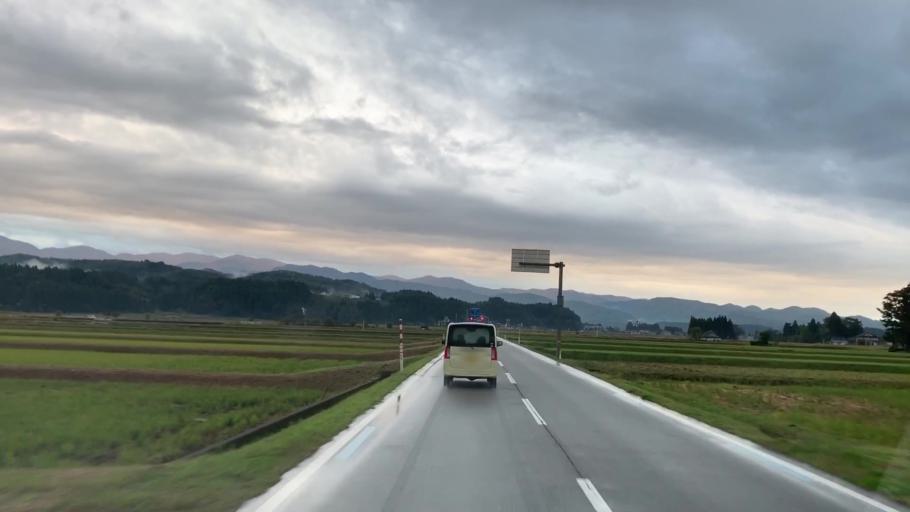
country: JP
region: Toyama
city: Kamiichi
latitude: 36.6289
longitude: 137.3286
